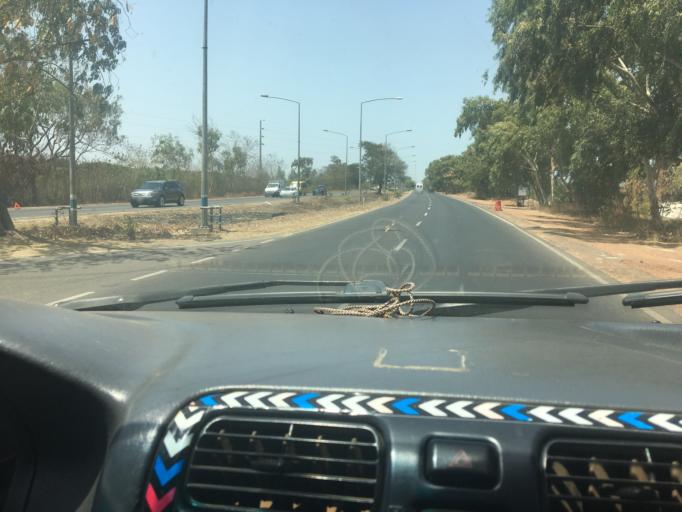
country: GM
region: Banjul
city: Bakau
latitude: 13.4693
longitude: -16.6405
